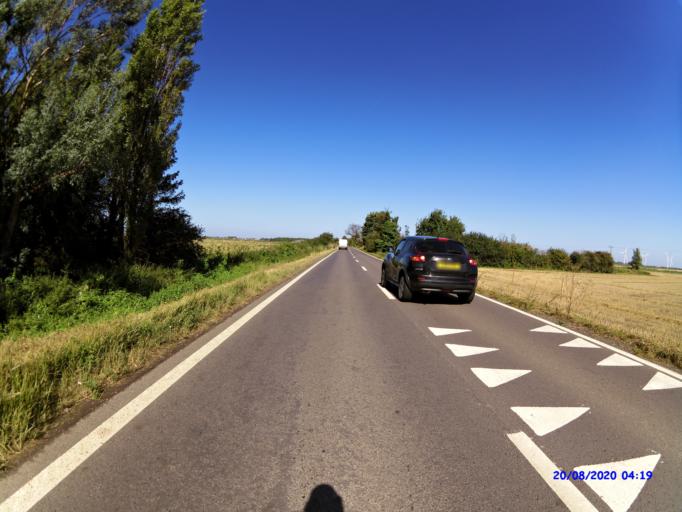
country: GB
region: England
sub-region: Cambridgeshire
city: Ramsey
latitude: 52.4921
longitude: -0.1182
